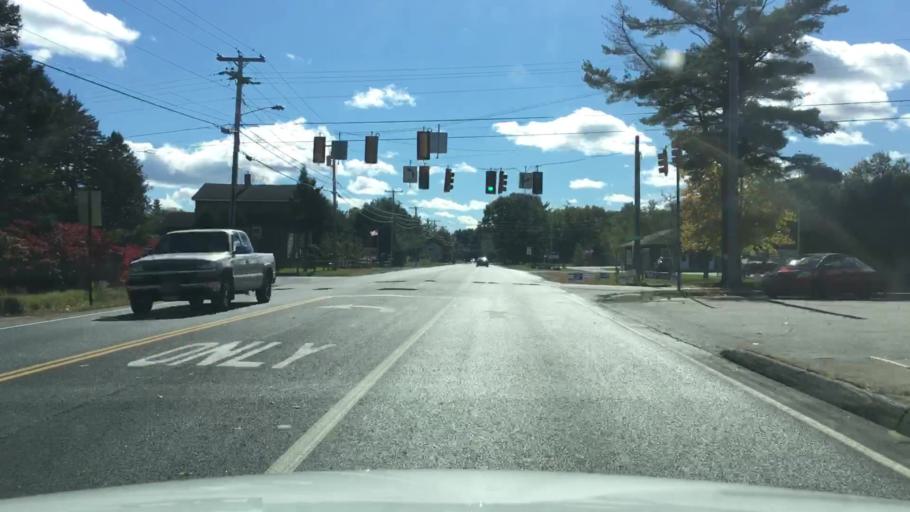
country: US
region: Maine
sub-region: York County
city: South Sanford
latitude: 43.4394
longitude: -70.7325
